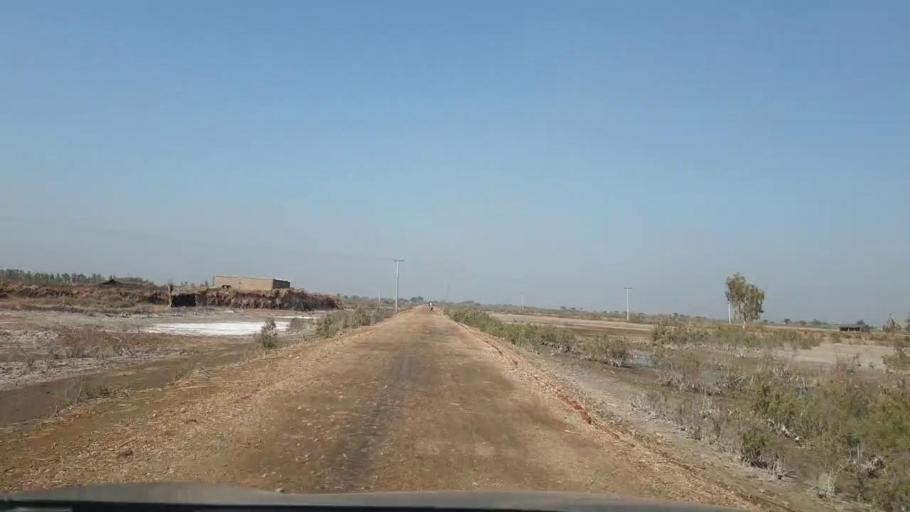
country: PK
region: Sindh
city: Berani
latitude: 25.6877
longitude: 68.8870
